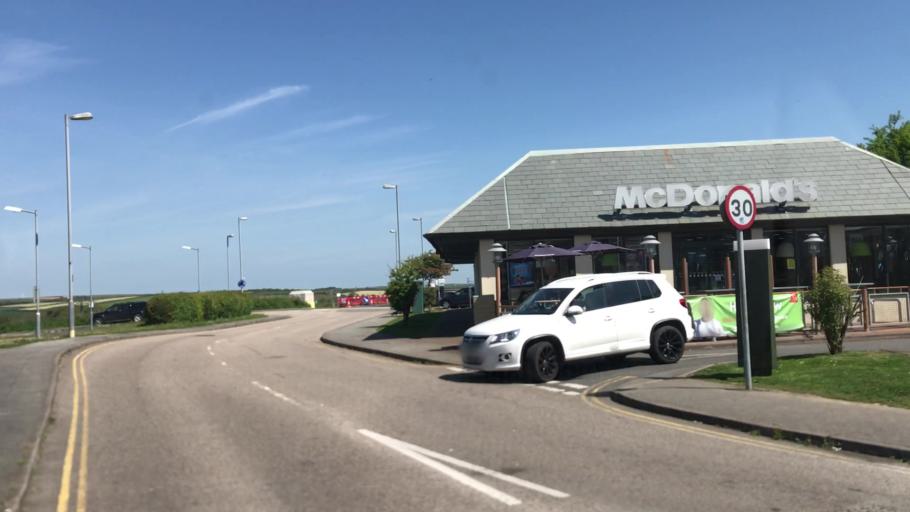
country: GB
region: England
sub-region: Cornwall
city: Truro
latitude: 50.2642
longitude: -5.1030
